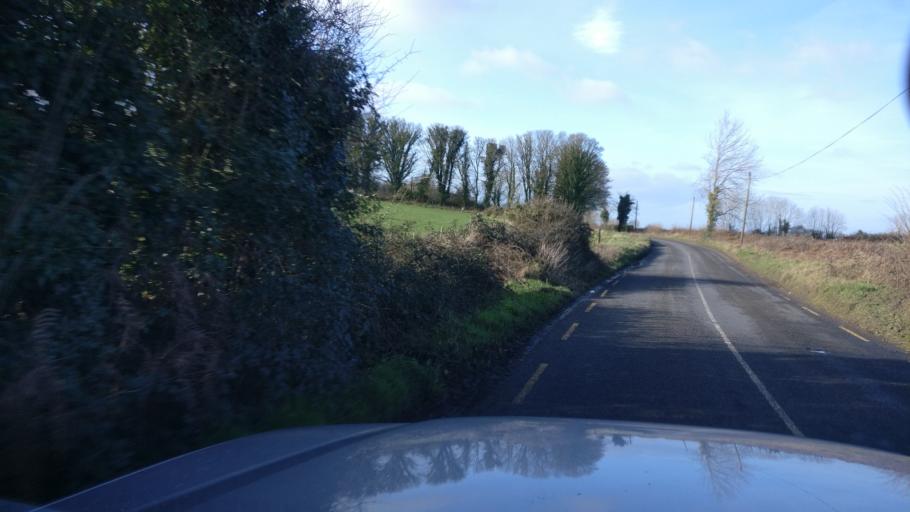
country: IE
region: Leinster
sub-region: Laois
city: Portlaoise
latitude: 53.0080
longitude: -7.2344
